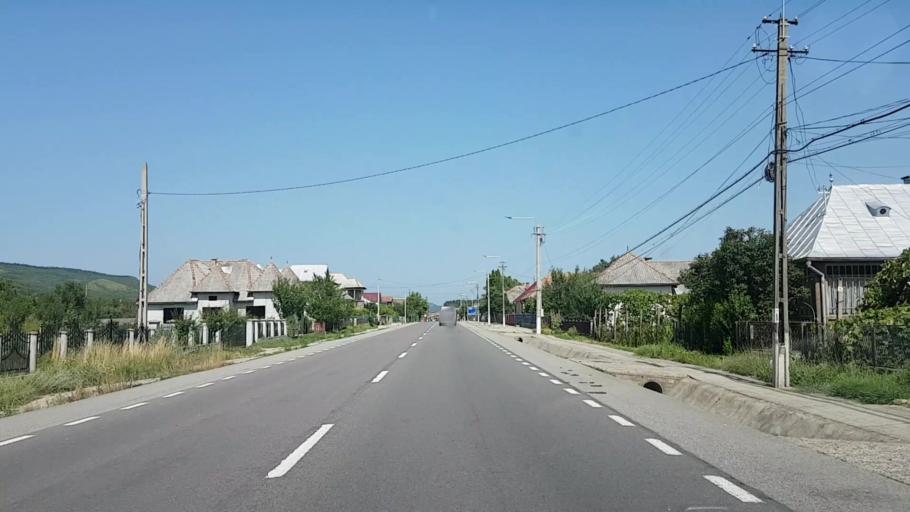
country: RO
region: Bistrita-Nasaud
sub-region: Comuna Petru Rares
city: Reteag
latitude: 47.1905
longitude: 24.0044
